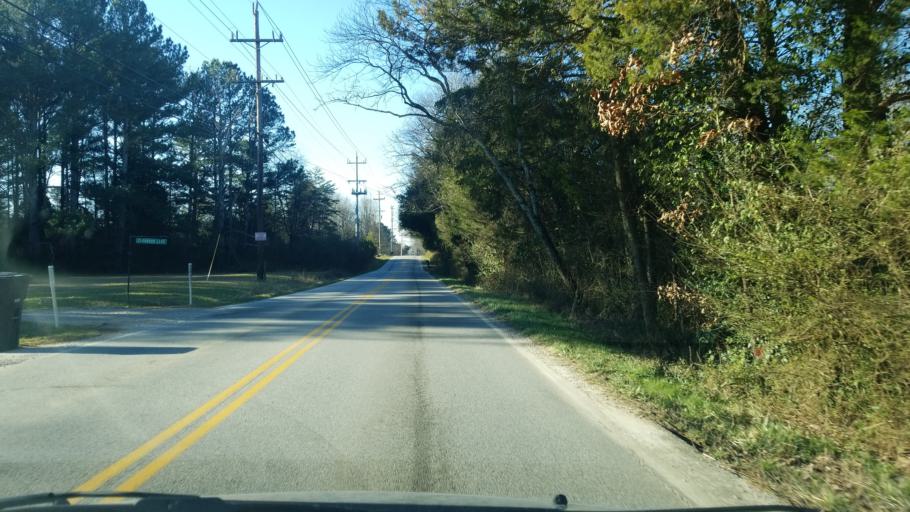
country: US
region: Tennessee
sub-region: Hamilton County
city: Collegedale
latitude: 35.0363
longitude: -85.0780
